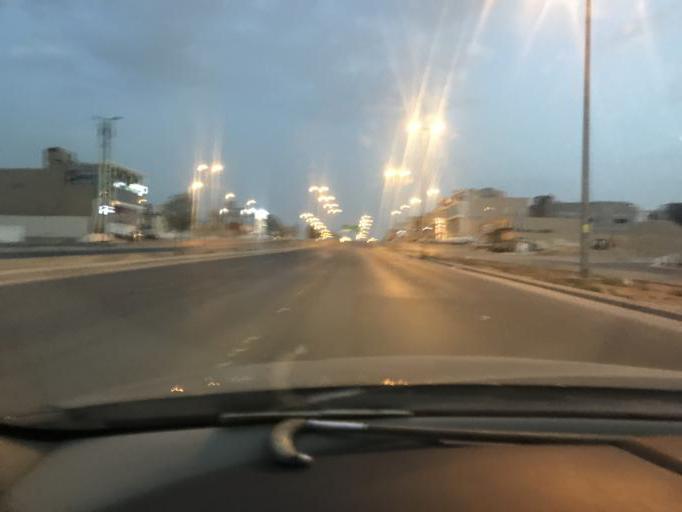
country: SA
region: Ar Riyad
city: Riyadh
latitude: 24.8423
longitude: 46.6754
